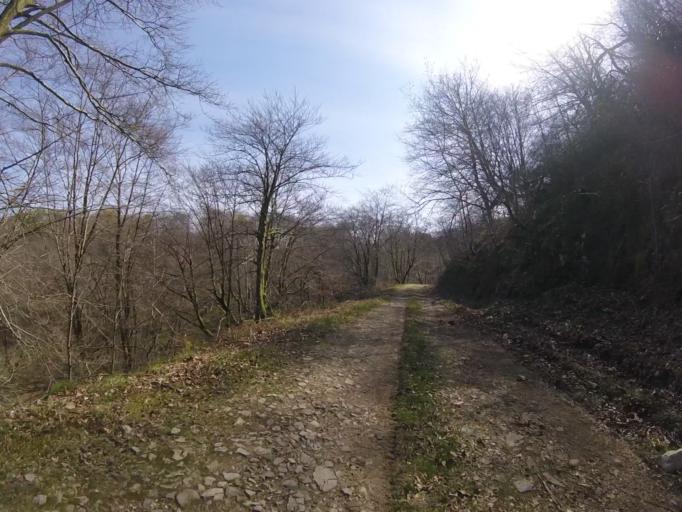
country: ES
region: Basque Country
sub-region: Provincia de Guipuzcoa
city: Irun
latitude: 43.2532
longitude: -1.8136
